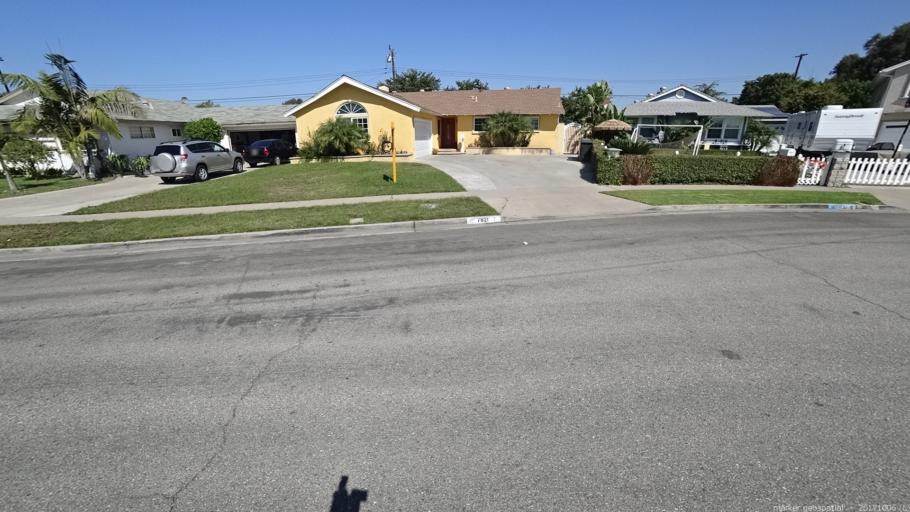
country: US
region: California
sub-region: Orange County
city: Stanton
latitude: 33.7862
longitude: -117.9957
